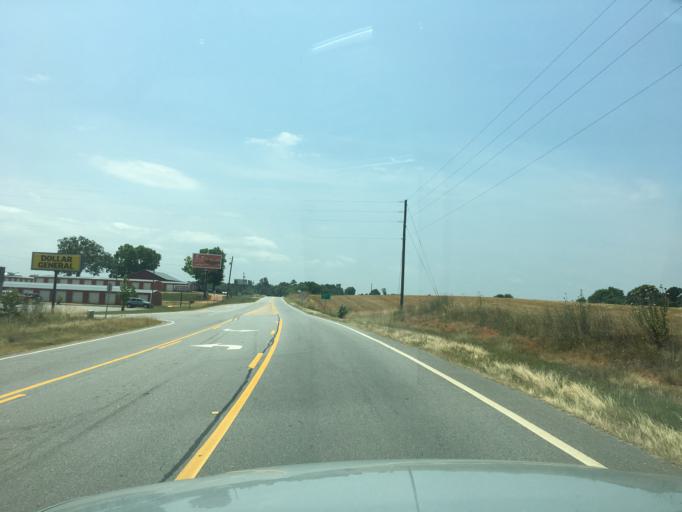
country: US
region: Georgia
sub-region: Hart County
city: Royston
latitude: 34.2853
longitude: -83.1608
